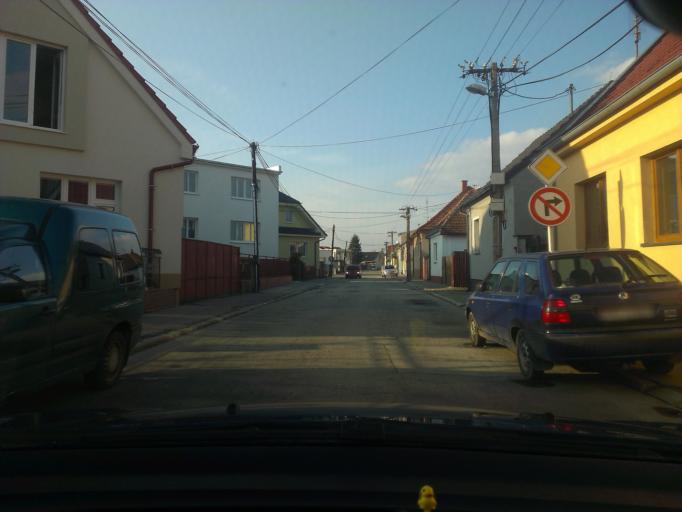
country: SK
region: Trnavsky
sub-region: Okres Trnava
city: Piestany
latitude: 48.6002
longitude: 17.8241
